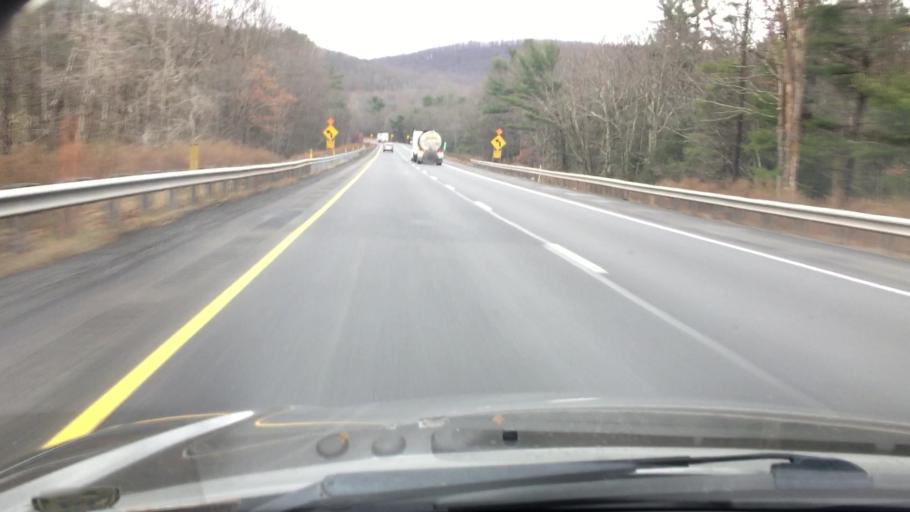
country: US
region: Pennsylvania
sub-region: Luzerne County
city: Freeland
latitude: 41.0598
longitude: -75.8627
